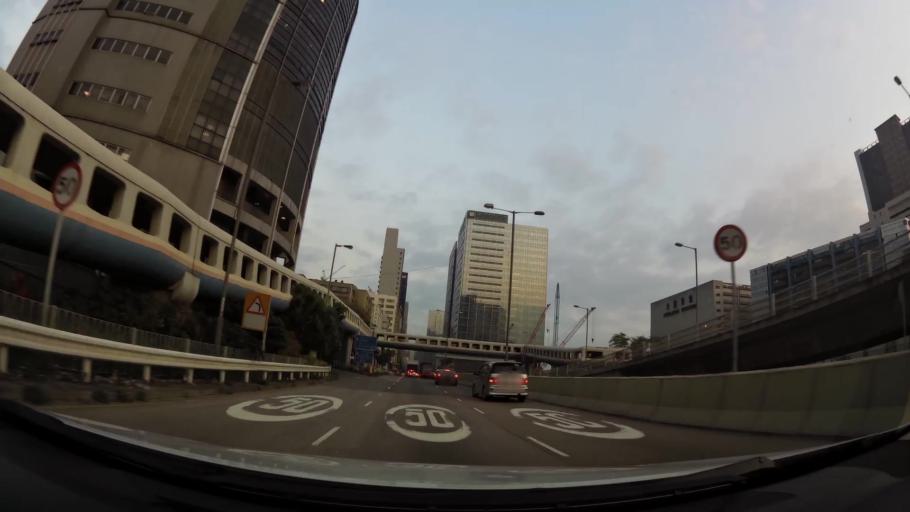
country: HK
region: Kowloon City
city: Kowloon
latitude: 22.3180
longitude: 114.2129
